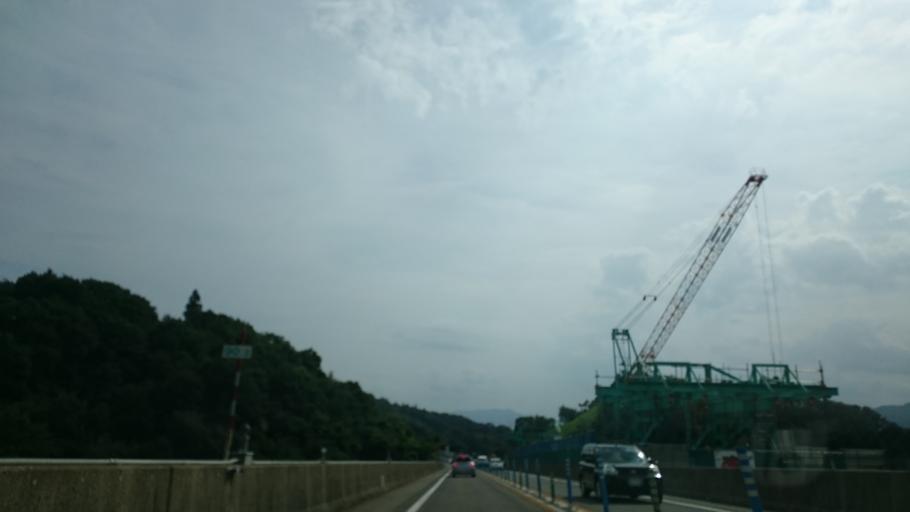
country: JP
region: Gifu
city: Gujo
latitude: 35.9803
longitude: 136.9011
